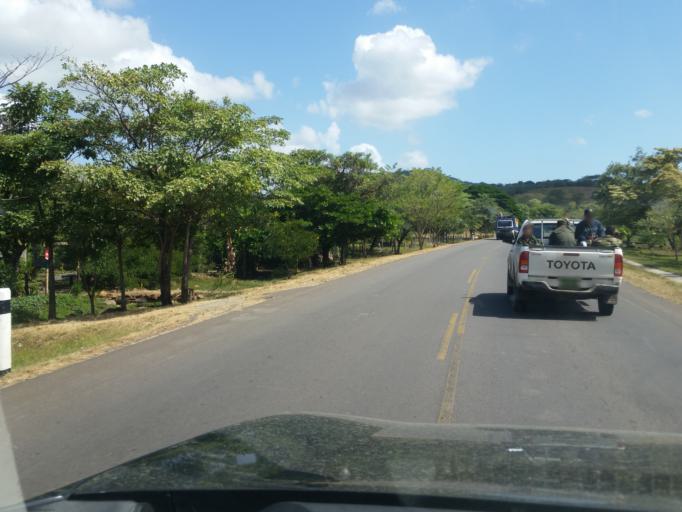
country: NI
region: Chontales
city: Comalapa
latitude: 12.1912
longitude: -85.6076
